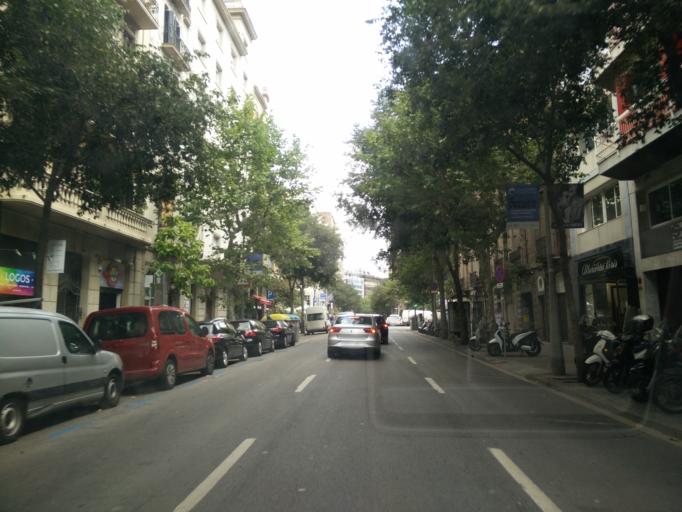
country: ES
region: Catalonia
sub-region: Provincia de Barcelona
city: Barcelona
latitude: 41.3935
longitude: 2.1532
